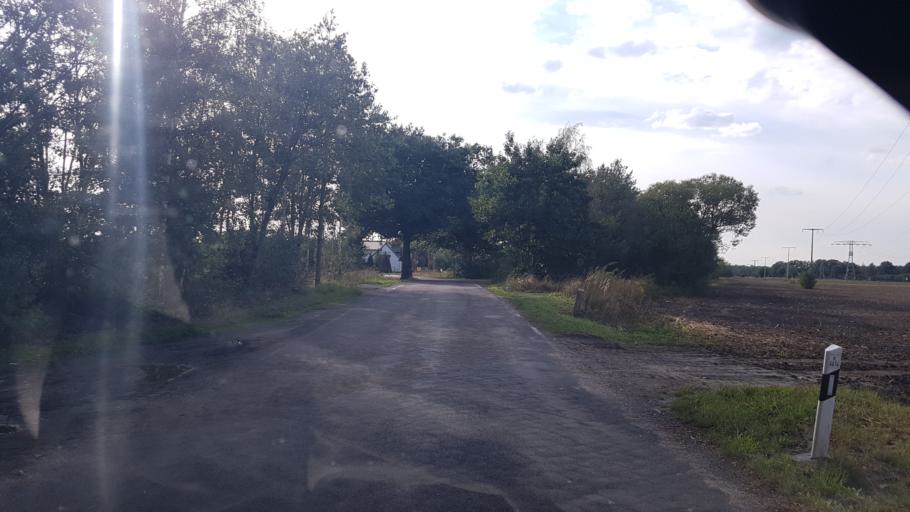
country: DE
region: Brandenburg
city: Welzow
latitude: 51.5567
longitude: 14.1399
